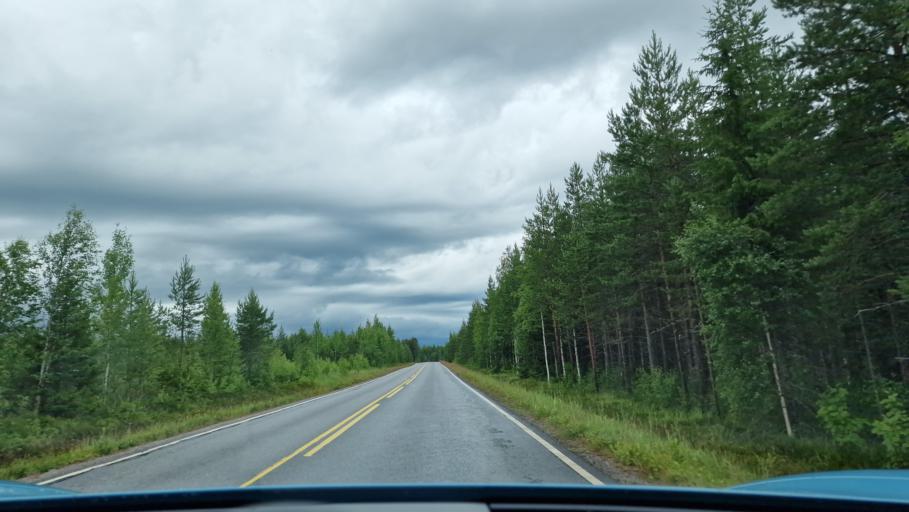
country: FI
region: Southern Ostrobothnia
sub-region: Jaerviseutu
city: Soini
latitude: 62.7125
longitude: 24.4400
